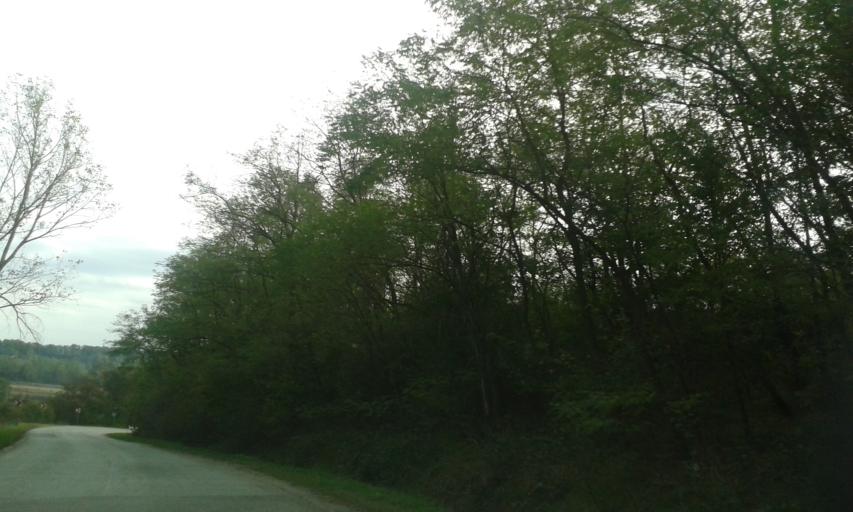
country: RO
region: Gorj
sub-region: Comuna Targu Carbunesti
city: Pojogeni
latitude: 44.9861
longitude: 23.4973
